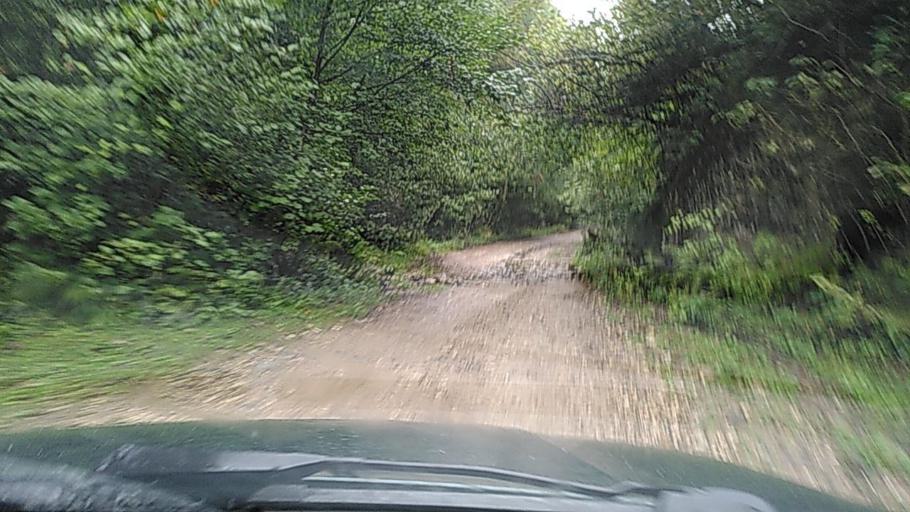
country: RU
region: Kabardino-Balkariya
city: Belaya Rechka
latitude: 43.4041
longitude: 43.4640
